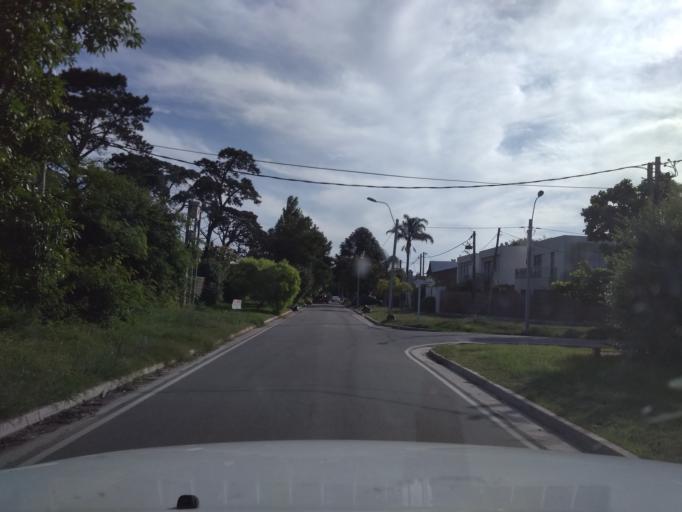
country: UY
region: Canelones
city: Barra de Carrasco
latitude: -34.8694
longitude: -56.0360
